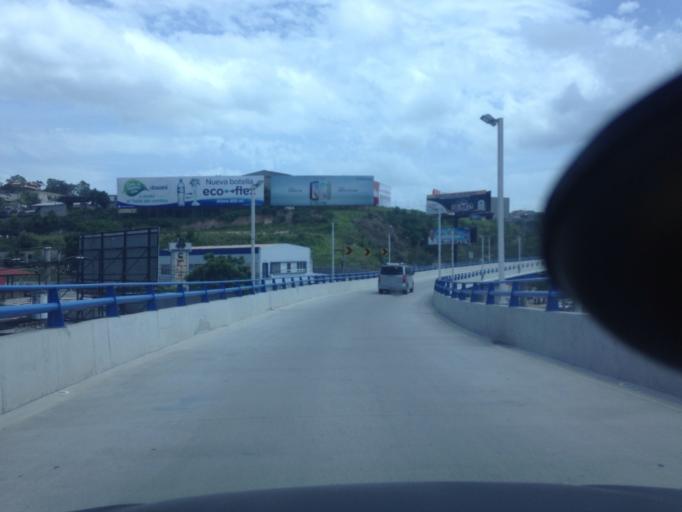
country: HN
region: Francisco Morazan
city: Tegucigalpa
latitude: 14.0713
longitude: -87.2142
